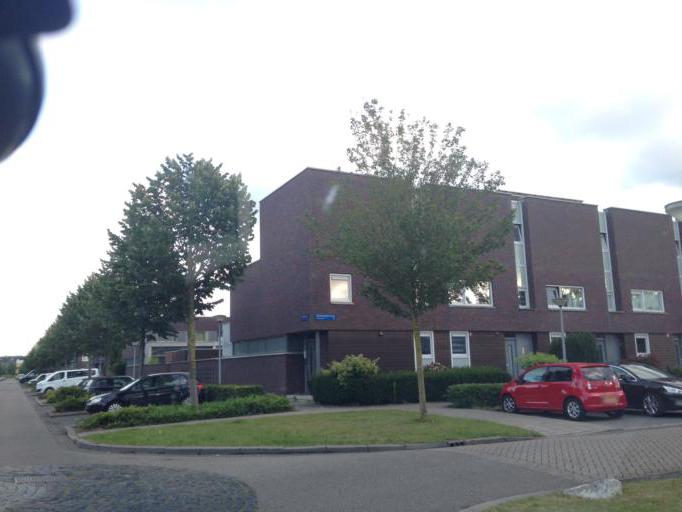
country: NL
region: Flevoland
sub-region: Gemeente Almere
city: Almere Stad
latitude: 52.3703
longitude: 5.2635
